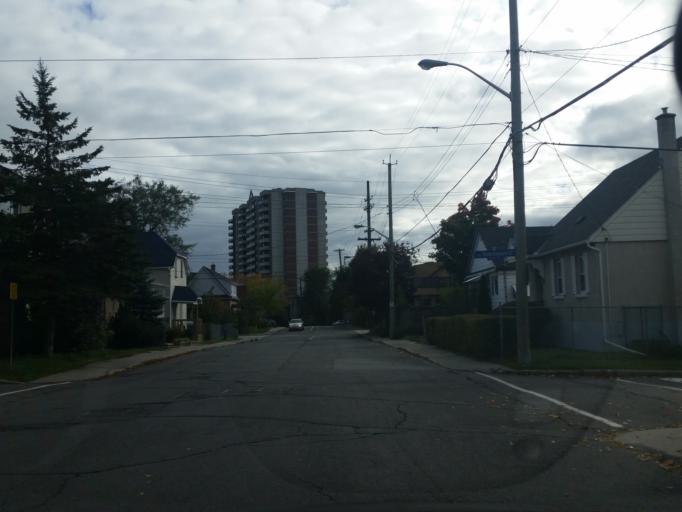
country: CA
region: Ontario
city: Ottawa
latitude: 45.4400
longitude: -75.6567
